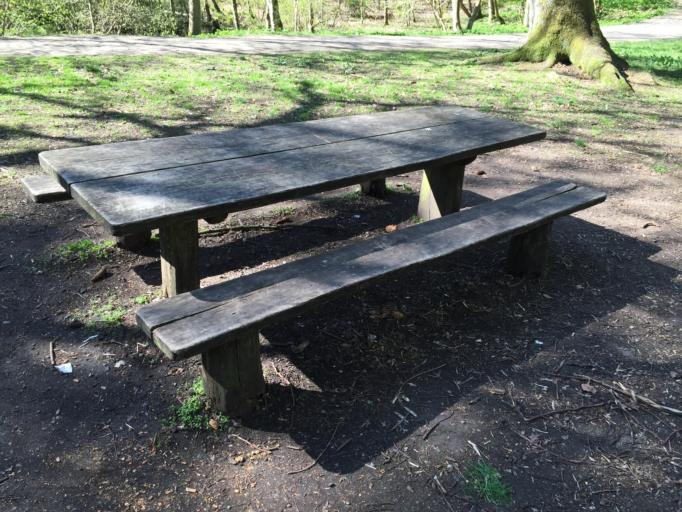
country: DK
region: Capital Region
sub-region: Fureso Kommune
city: Vaerlose
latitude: 55.7575
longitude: 12.3819
